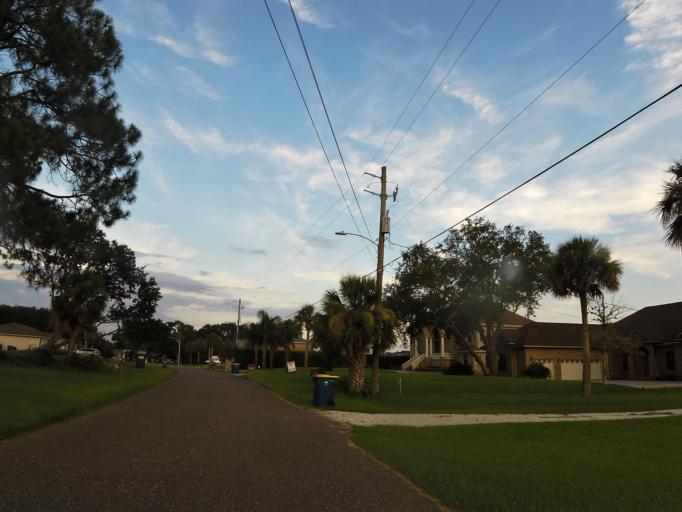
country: US
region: Florida
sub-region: Duval County
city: Atlantic Beach
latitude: 30.3939
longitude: -81.5015
